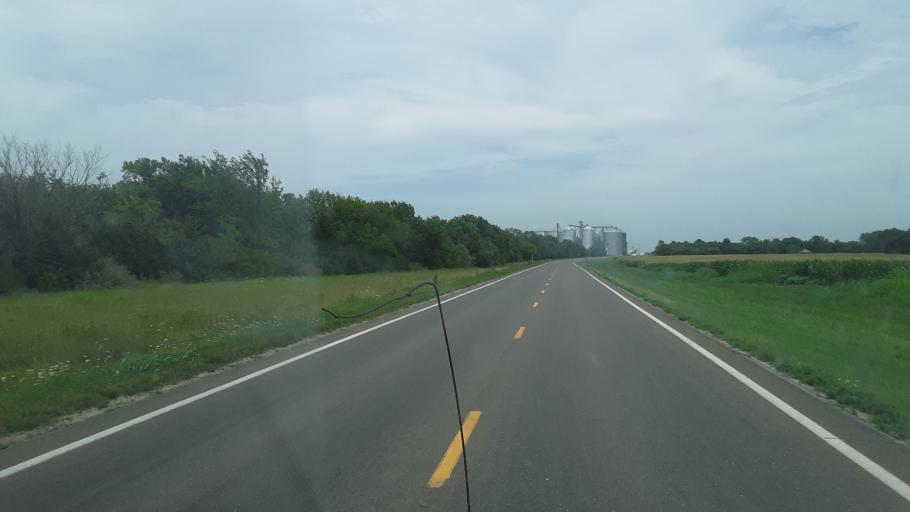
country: US
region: Kansas
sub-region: Allen County
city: Iola
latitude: 37.9190
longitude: -95.5454
